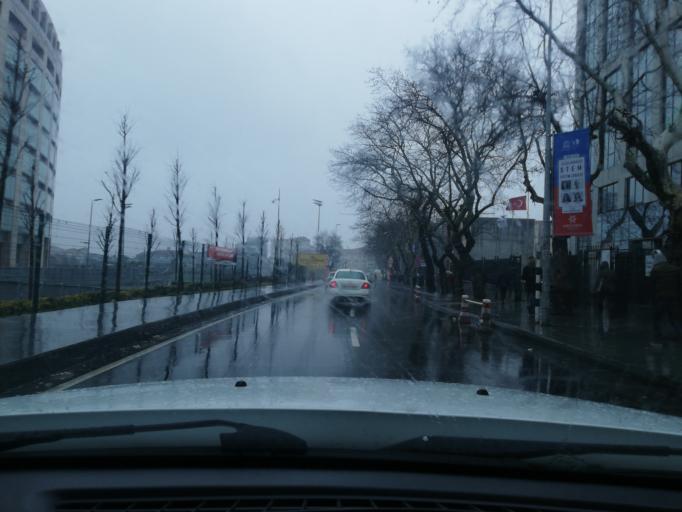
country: TR
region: Istanbul
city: Sisli
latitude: 41.0696
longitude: 28.9821
